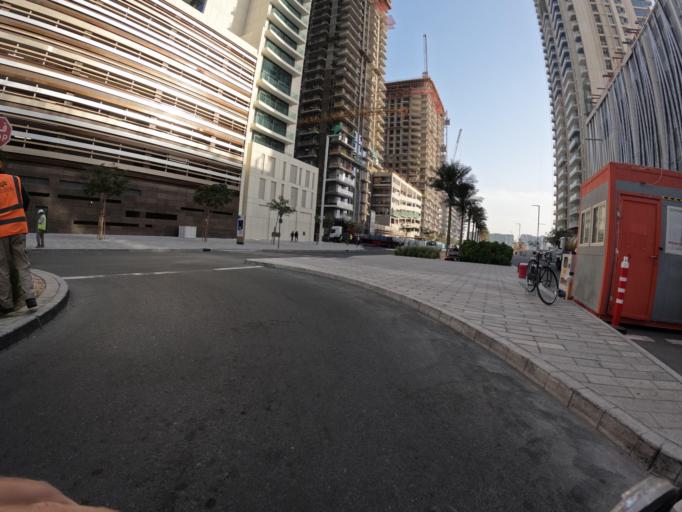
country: AE
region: Dubai
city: Dubai
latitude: 25.0980
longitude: 55.1402
